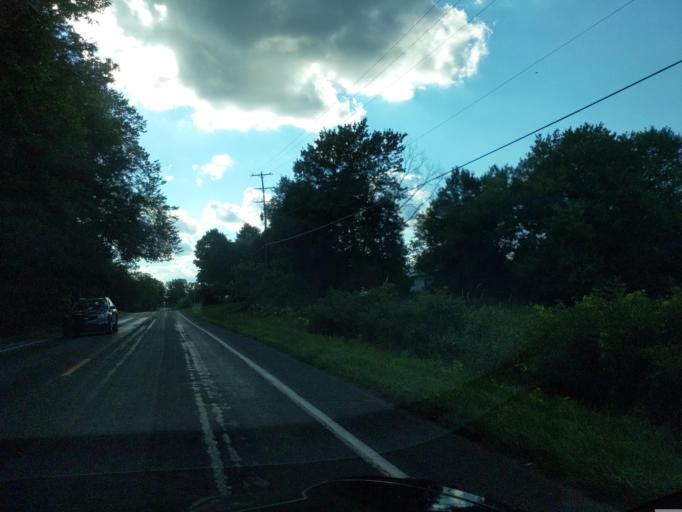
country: US
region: Michigan
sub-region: Ingham County
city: Holt
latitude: 42.5822
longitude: -84.5362
